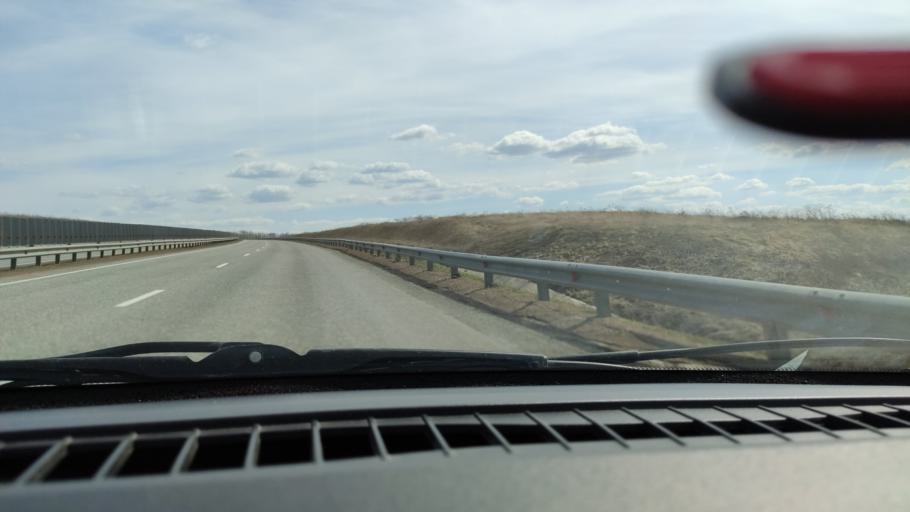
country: RU
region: Bashkortostan
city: Kushnarenkovo
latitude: 55.0644
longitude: 55.3123
